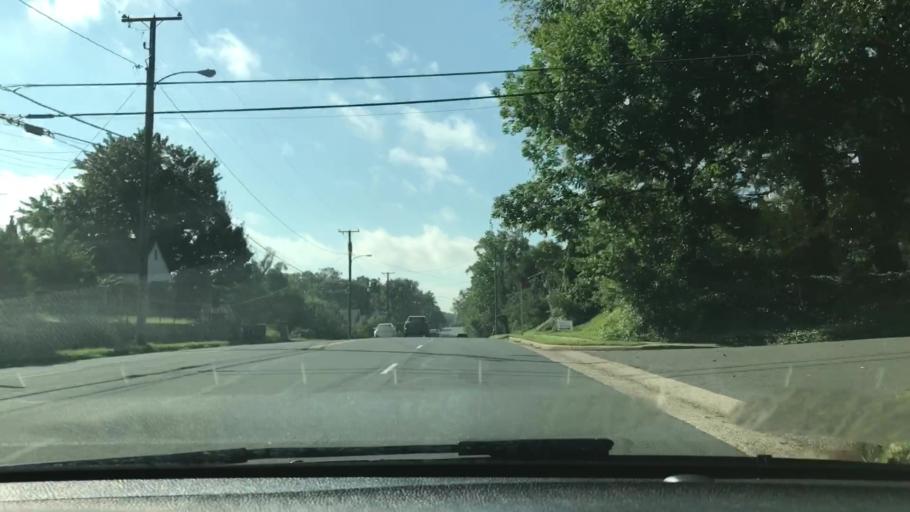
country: US
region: Virginia
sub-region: Fairfax County
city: Annandale
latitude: 38.8396
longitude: -77.1991
